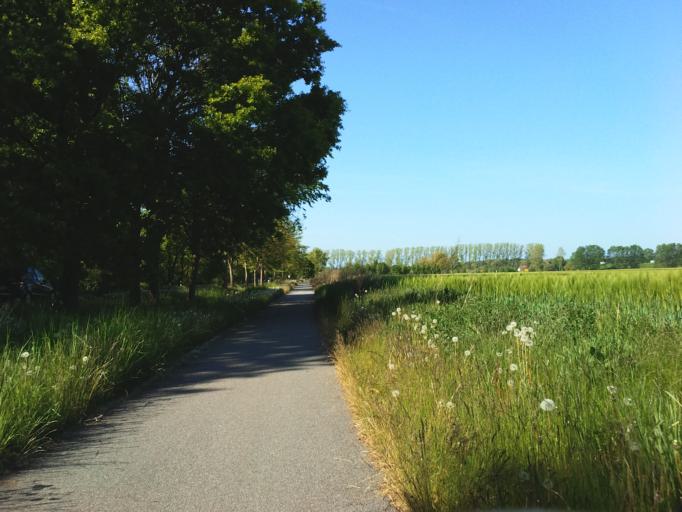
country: DE
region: Mecklenburg-Vorpommern
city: Monchhagen
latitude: 54.1717
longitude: 12.2013
